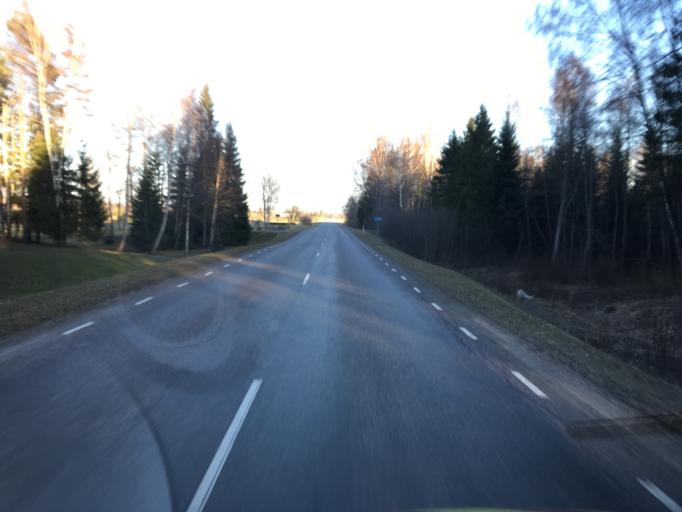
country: EE
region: Raplamaa
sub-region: Rapla vald
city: Rapla
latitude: 59.0866
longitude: 24.8124
